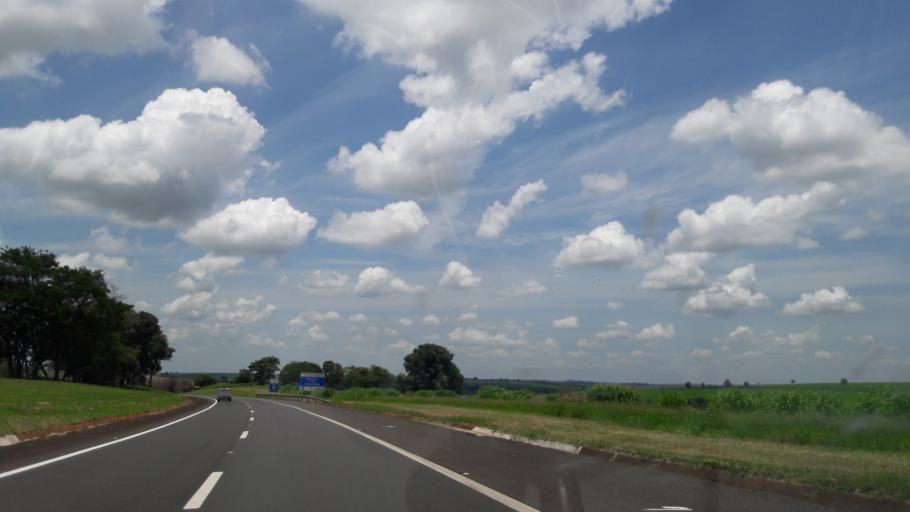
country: BR
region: Sao Paulo
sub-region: Avare
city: Avare
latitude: -22.9547
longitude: -48.8241
